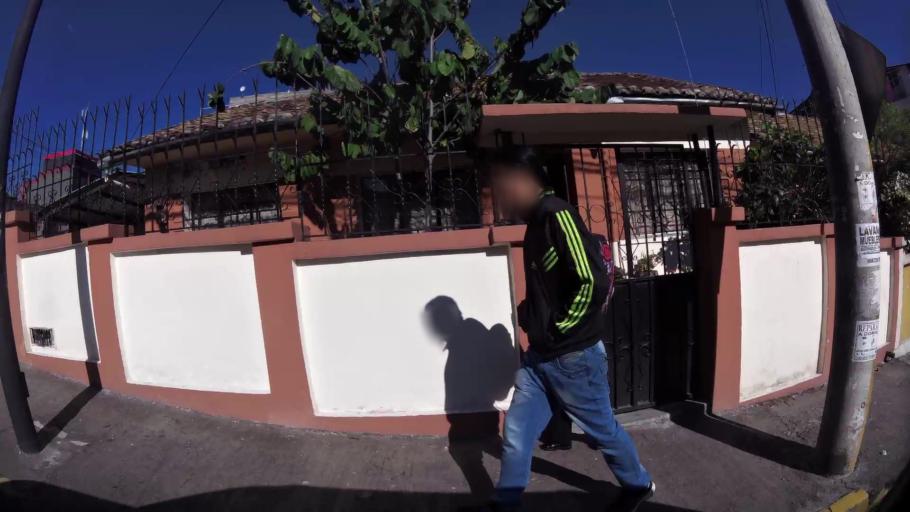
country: EC
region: Pichincha
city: Quito
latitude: -0.2459
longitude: -78.5225
